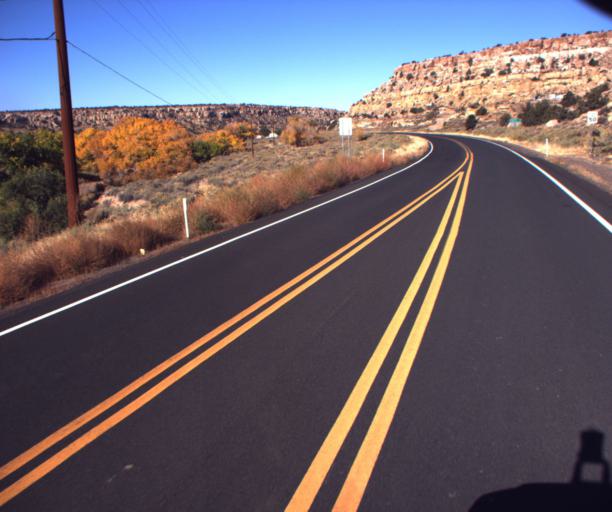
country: US
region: Arizona
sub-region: Navajo County
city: First Mesa
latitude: 35.8158
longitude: -110.2066
